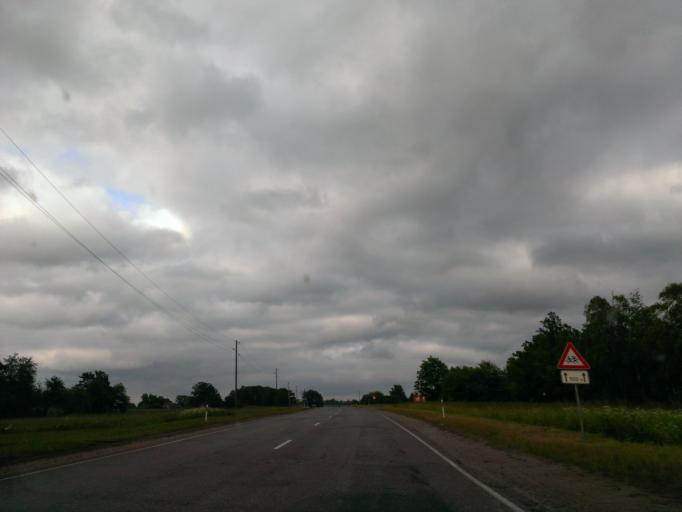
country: LV
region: Skrunda
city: Skrunda
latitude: 56.6772
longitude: 22.2131
